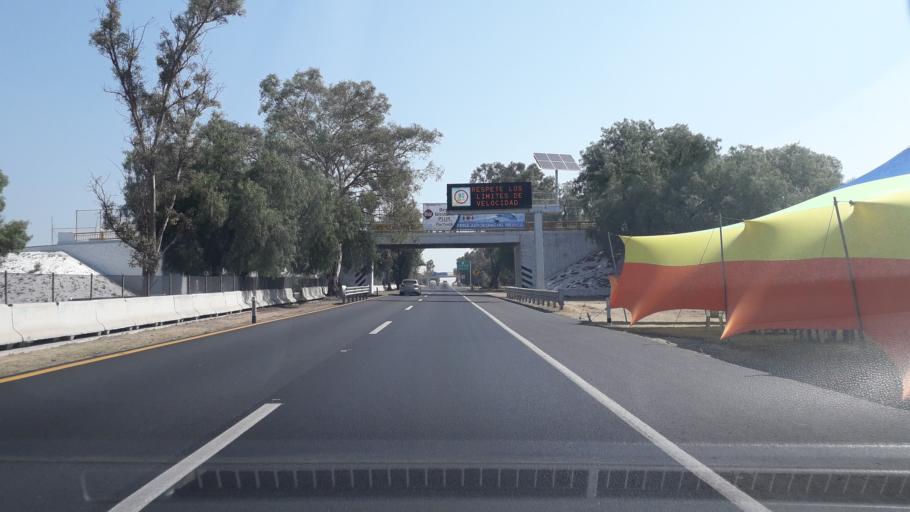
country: MX
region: Mexico
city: Santo Tomas Chiconautla
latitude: 19.6535
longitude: -99.0110
